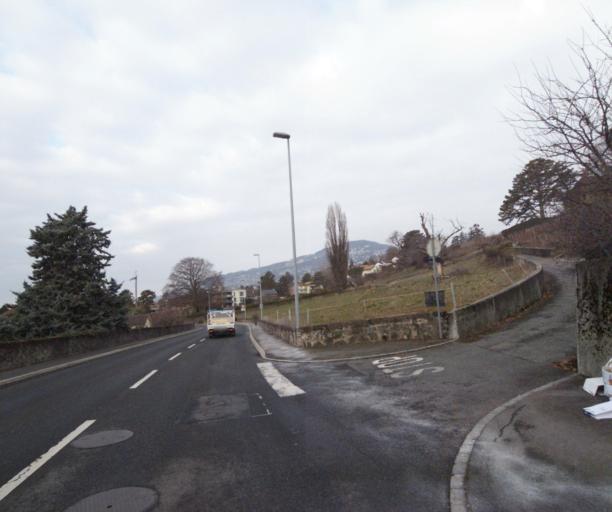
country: CH
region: Vaud
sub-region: Riviera-Pays-d'Enhaut District
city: La Tour-de-Peilz
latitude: 46.4615
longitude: 6.8623
